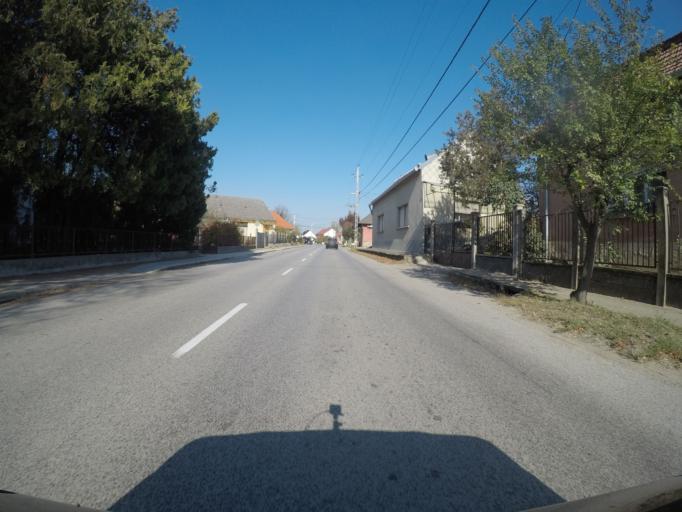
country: HU
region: Tolna
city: Nagydorog
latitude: 46.6214
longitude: 18.6559
